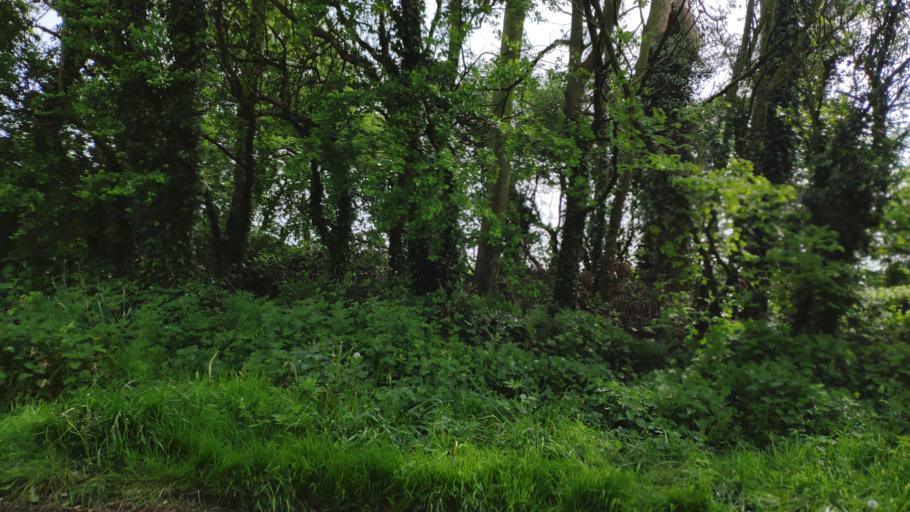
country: IE
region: Munster
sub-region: County Cork
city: Blarney
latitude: 51.9631
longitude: -8.5142
